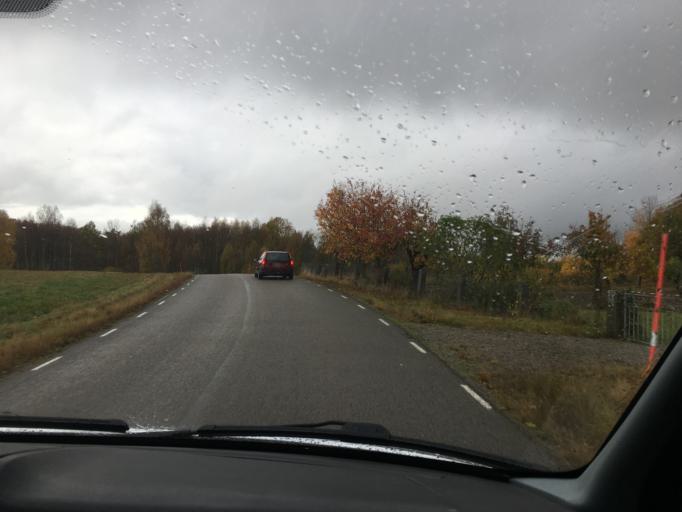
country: SE
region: Kronoberg
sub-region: Vaxjo Kommun
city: Ingelstad
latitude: 56.5991
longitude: 14.7600
